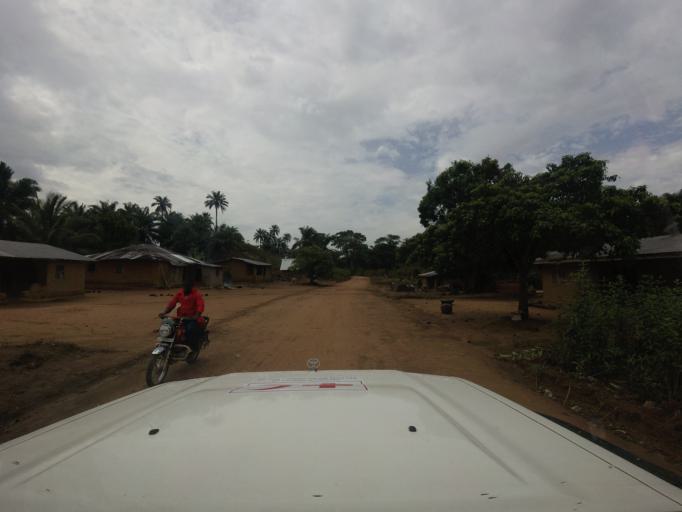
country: SL
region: Eastern Province
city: Buedu
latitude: 8.3385
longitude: -10.2076
